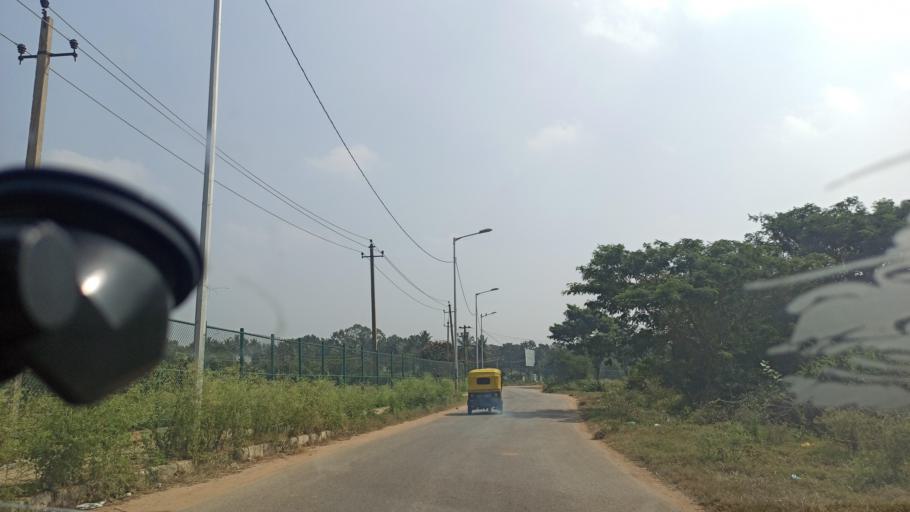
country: IN
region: Karnataka
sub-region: Bangalore Urban
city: Yelahanka
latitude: 13.0816
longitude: 77.6134
